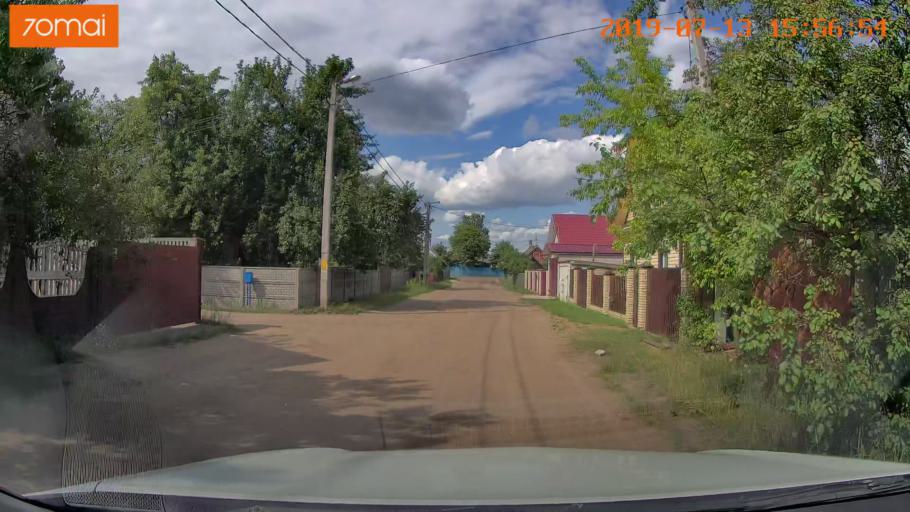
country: BY
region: Mogilev
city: Babruysk
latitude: 53.1457
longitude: 29.2025
